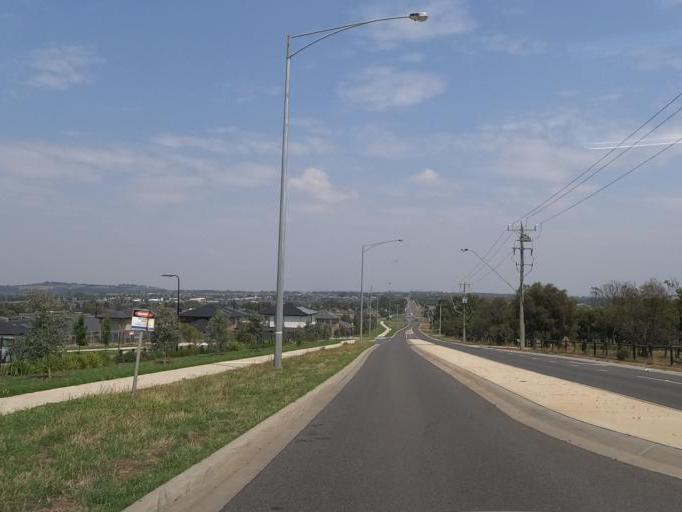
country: AU
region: Victoria
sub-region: Hume
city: Craigieburn
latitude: -37.5680
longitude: 144.9267
